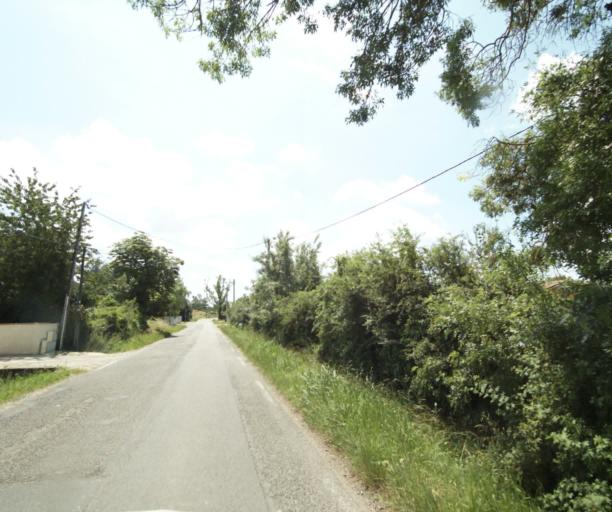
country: FR
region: Midi-Pyrenees
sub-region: Departement du Tarn-et-Garonne
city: Montauban
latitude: 44.0540
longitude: 1.3419
